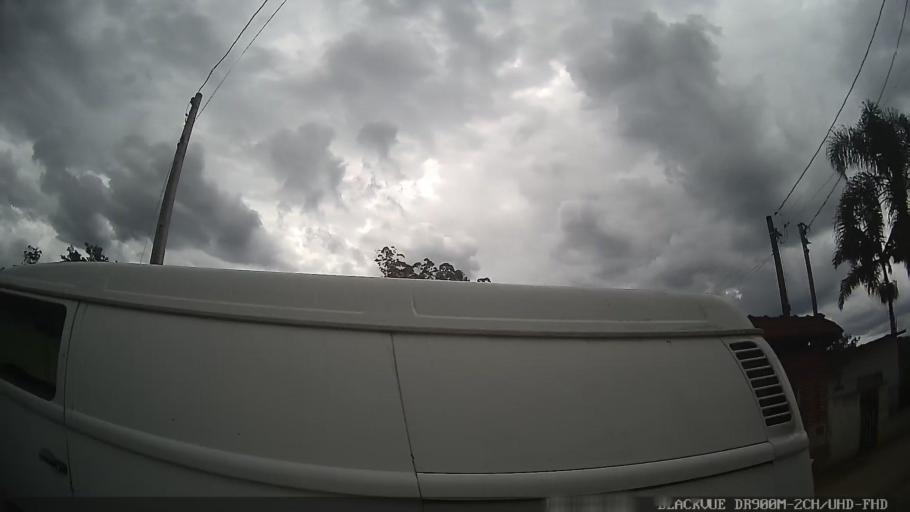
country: BR
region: Sao Paulo
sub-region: Suzano
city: Suzano
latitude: -23.6530
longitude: -46.3141
